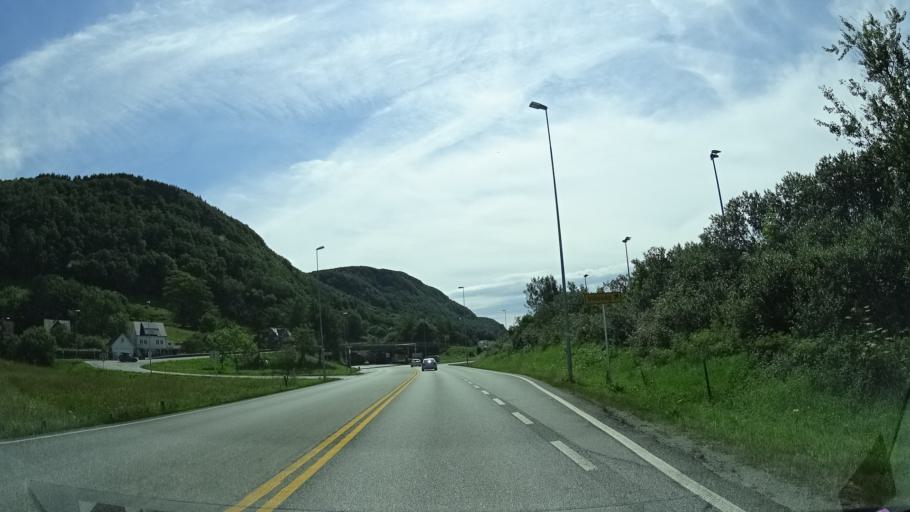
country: NO
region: Rogaland
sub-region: Rennesoy
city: Vikevag
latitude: 59.1073
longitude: 5.7008
